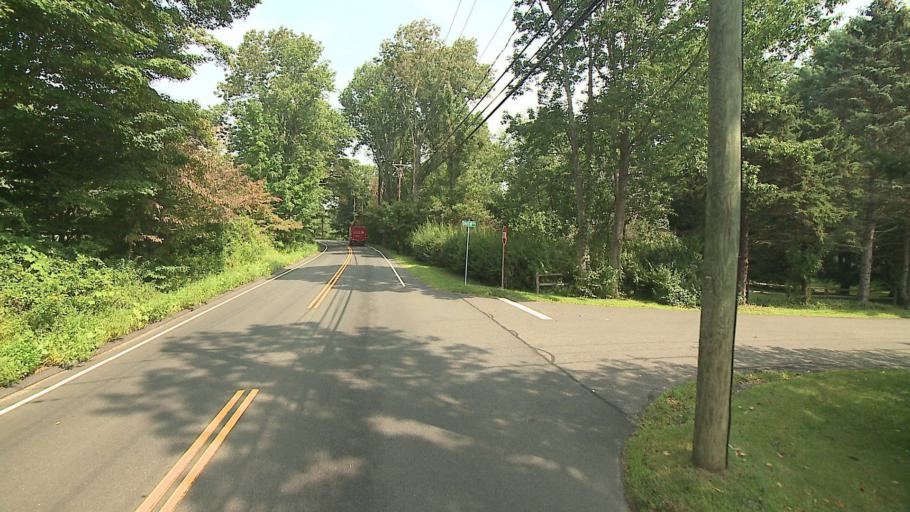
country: US
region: Connecticut
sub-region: Fairfield County
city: Bethel
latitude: 41.3259
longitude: -73.3876
